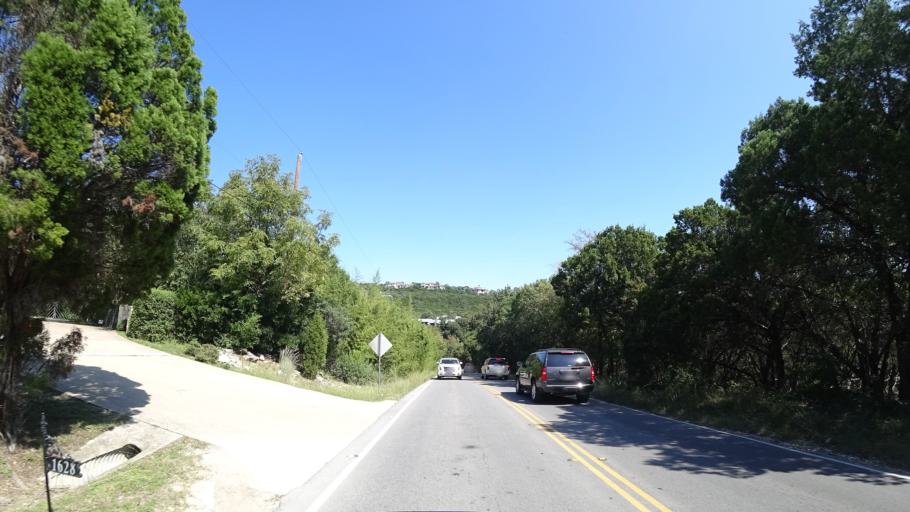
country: US
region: Texas
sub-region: Travis County
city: West Lake Hills
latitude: 30.3013
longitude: -97.7960
